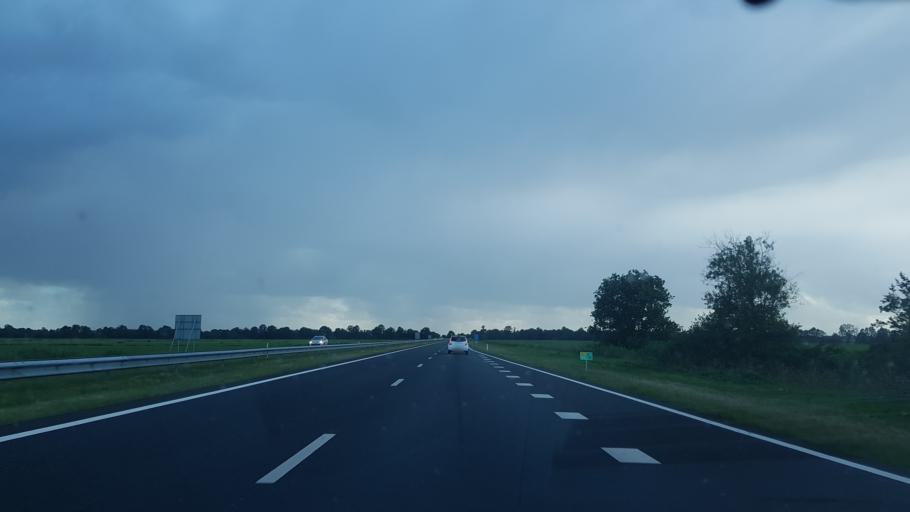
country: NL
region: Friesland
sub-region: Gemeente Smallingerland
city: Oudega
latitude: 53.1452
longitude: 6.0123
